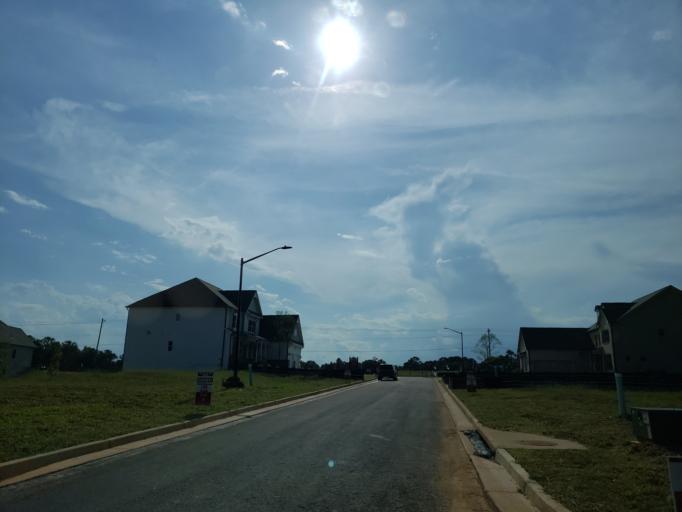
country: US
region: Georgia
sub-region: Cherokee County
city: Woodstock
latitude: 34.0435
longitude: -84.5101
